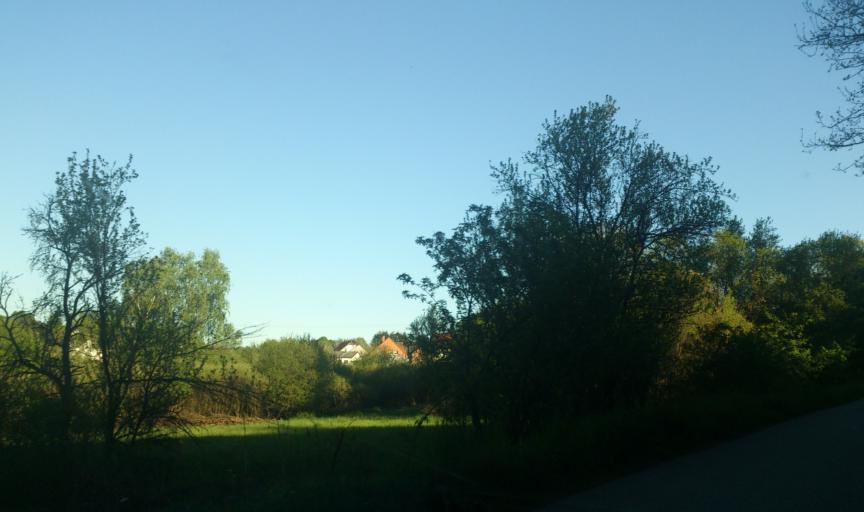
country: DE
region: Rheinland-Pfalz
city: Hahnweiler
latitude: 49.5326
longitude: 7.2150
